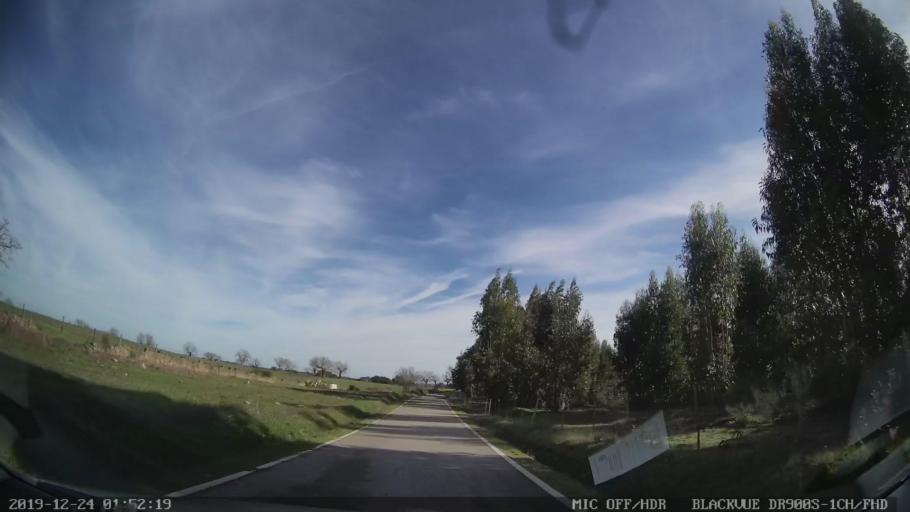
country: PT
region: Portalegre
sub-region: Nisa
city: Nisa
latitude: 39.4929
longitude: -7.7466
